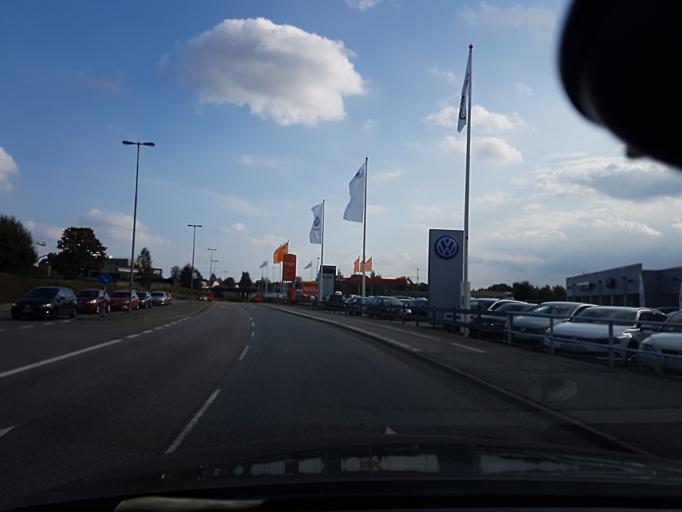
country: SE
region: Kronoberg
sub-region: Vaxjo Kommun
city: Vaexjoe
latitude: 56.8780
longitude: 14.7853
